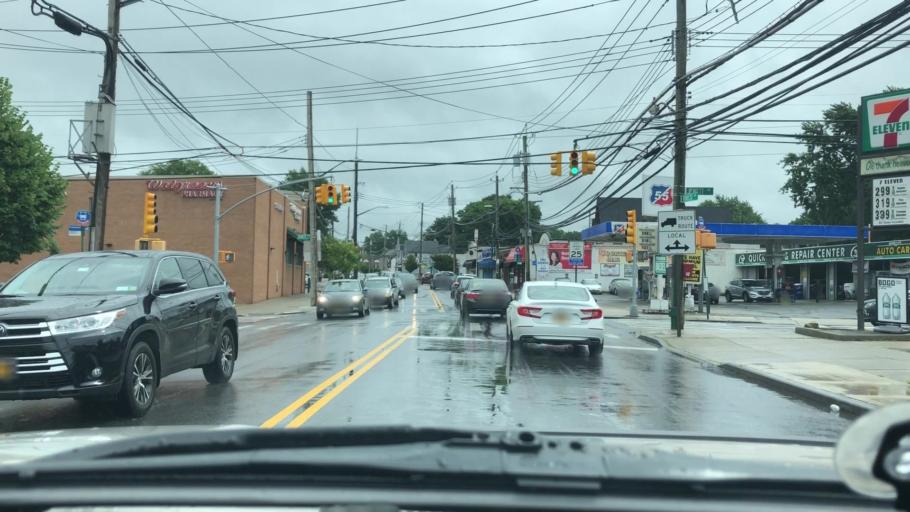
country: US
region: New Jersey
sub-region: Hudson County
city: Bayonne
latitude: 40.6264
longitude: -74.1317
